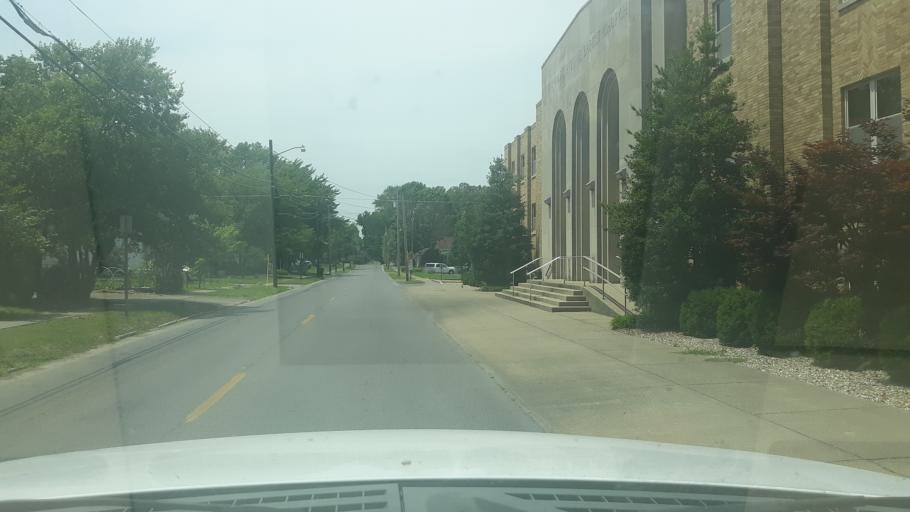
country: US
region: Illinois
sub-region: Saline County
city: Harrisburg
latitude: 37.7313
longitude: -88.5467
